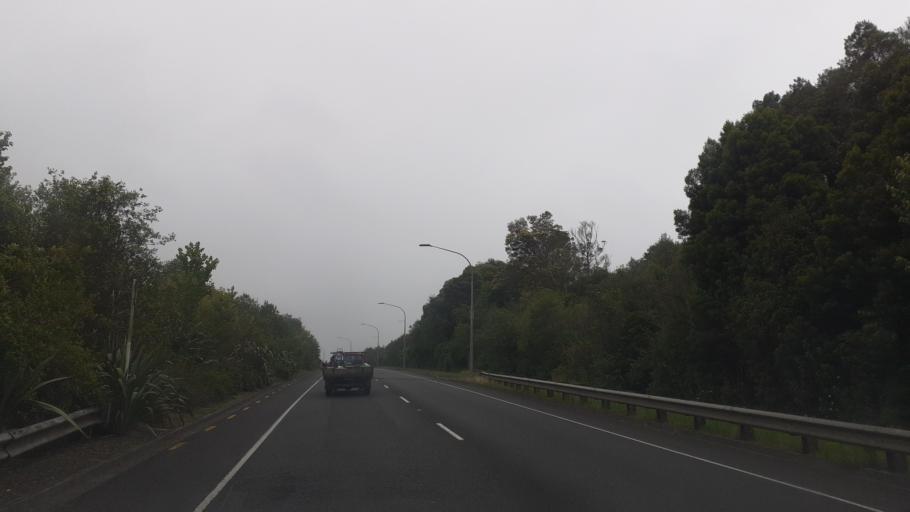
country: NZ
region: Northland
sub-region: Far North District
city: Kerikeri
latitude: -35.2158
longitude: 173.9521
